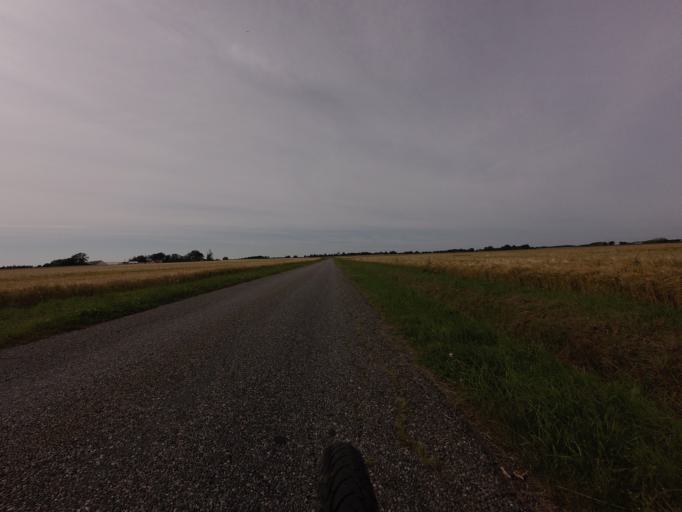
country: DK
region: North Denmark
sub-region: Hjorring Kommune
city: Hjorring
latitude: 57.4386
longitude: 9.8647
